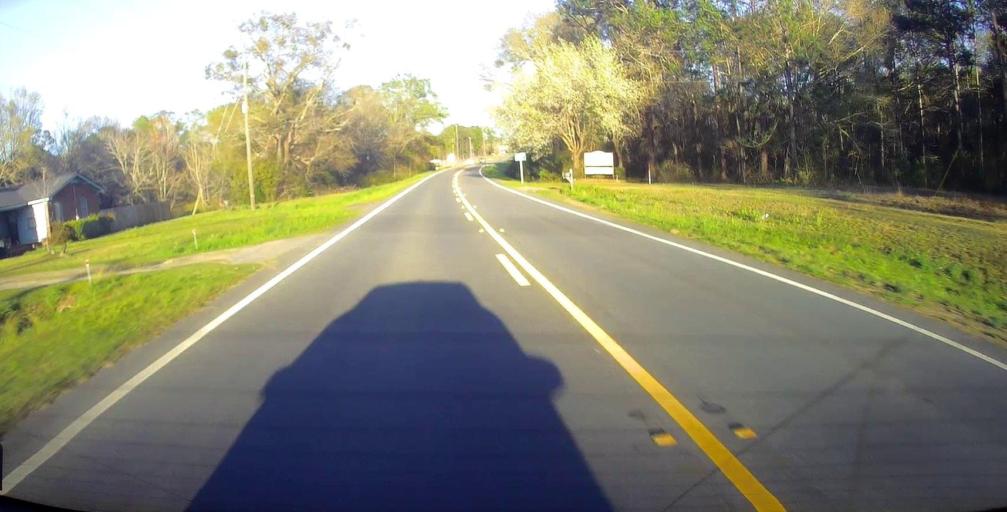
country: US
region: Georgia
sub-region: Wilcox County
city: Abbeville
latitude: 31.9921
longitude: -83.3183
